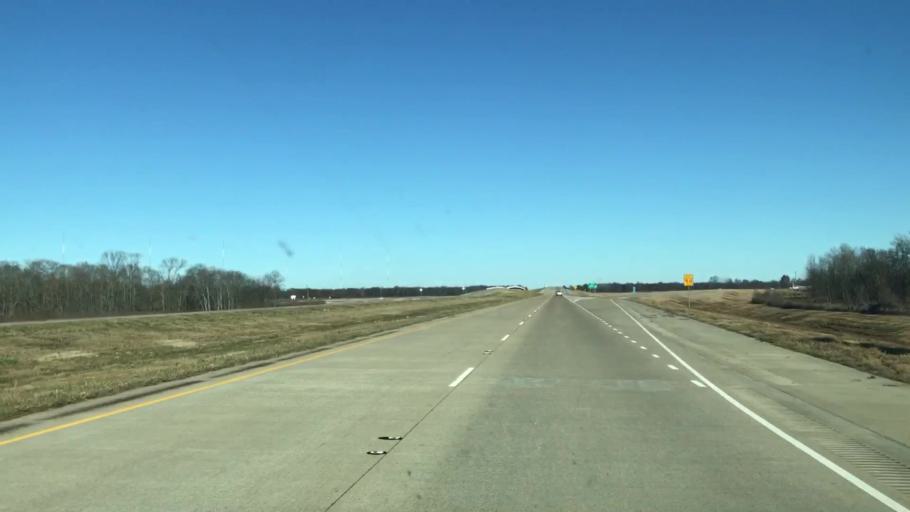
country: US
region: Louisiana
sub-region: Caddo Parish
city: Blanchard
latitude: 32.6693
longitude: -93.8477
